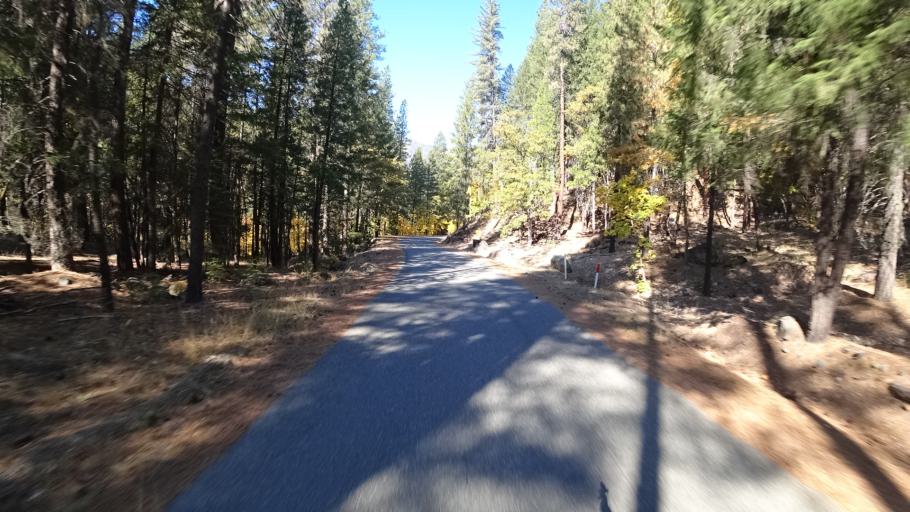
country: US
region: California
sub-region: Siskiyou County
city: Happy Camp
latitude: 41.6359
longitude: -123.1055
